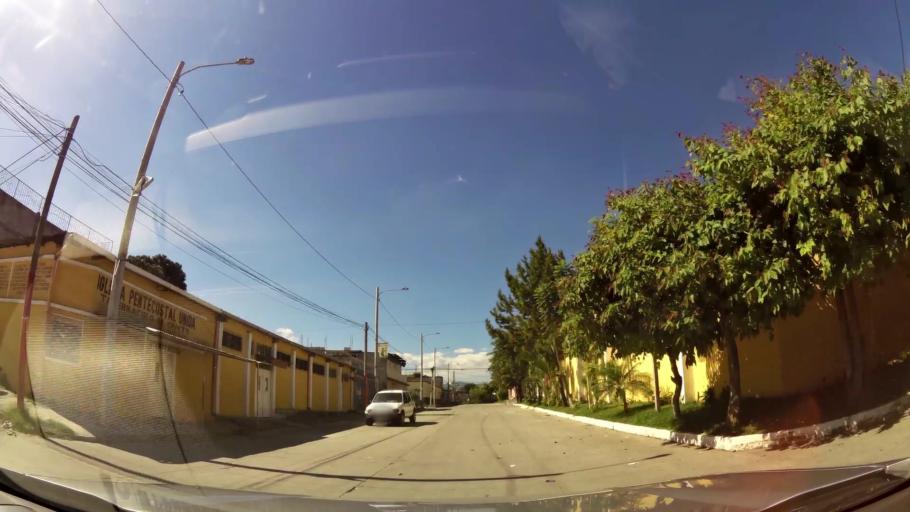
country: GT
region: Guatemala
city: Petapa
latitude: 14.5072
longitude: -90.5676
